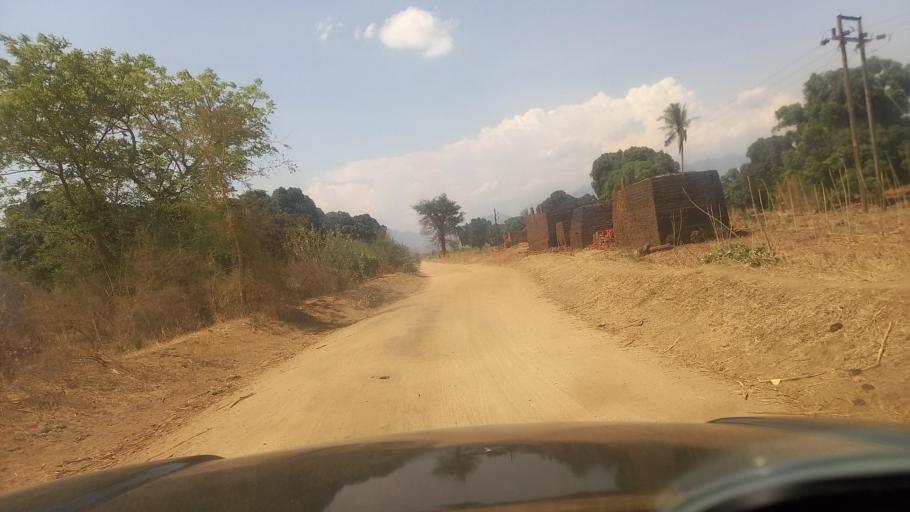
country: TZ
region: Morogoro
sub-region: Mvomero District
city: Mvomero
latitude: -6.3634
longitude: 37.4385
